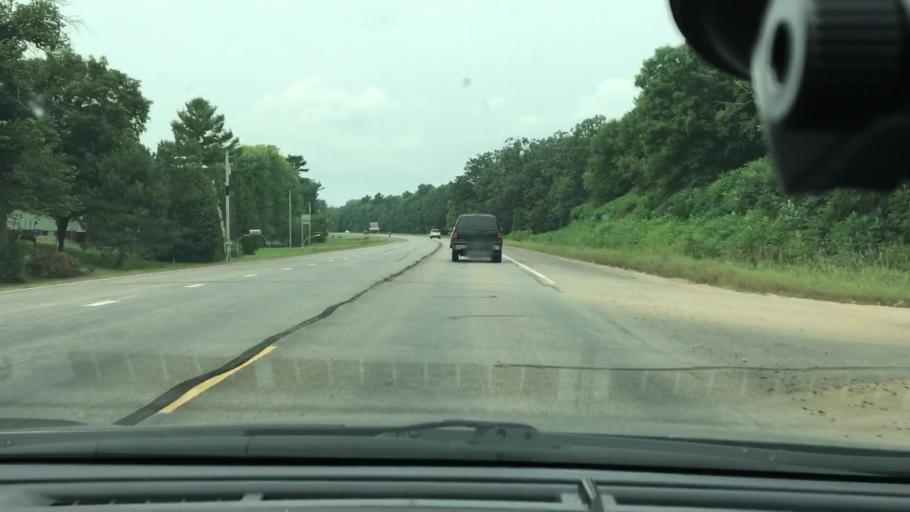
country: US
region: Minnesota
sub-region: Mille Lacs County
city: Vineland
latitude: 46.3268
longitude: -93.7849
